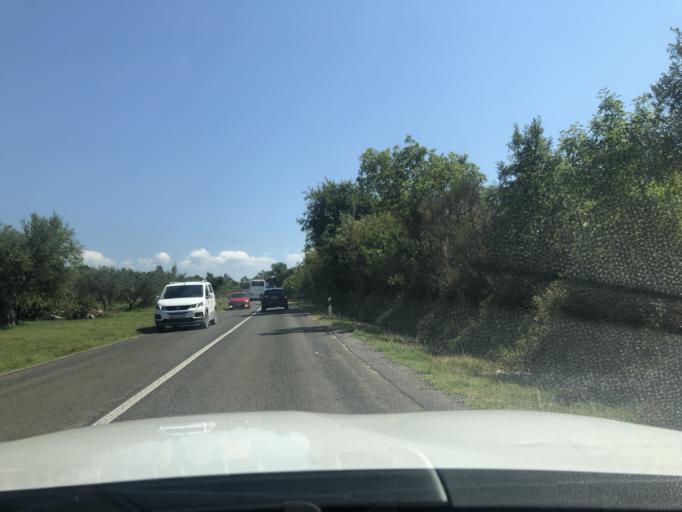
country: HR
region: Istarska
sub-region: Grad Rovinj
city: Rovinj
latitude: 45.0414
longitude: 13.7557
